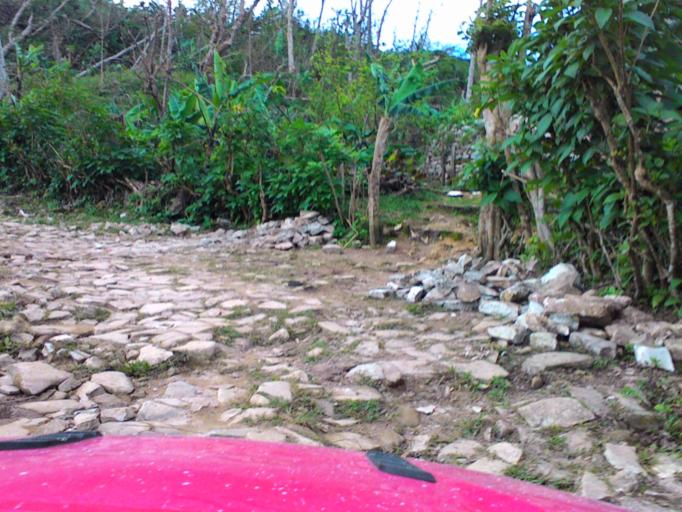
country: HT
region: Grandans
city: Moron
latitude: 18.4583
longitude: -74.1165
